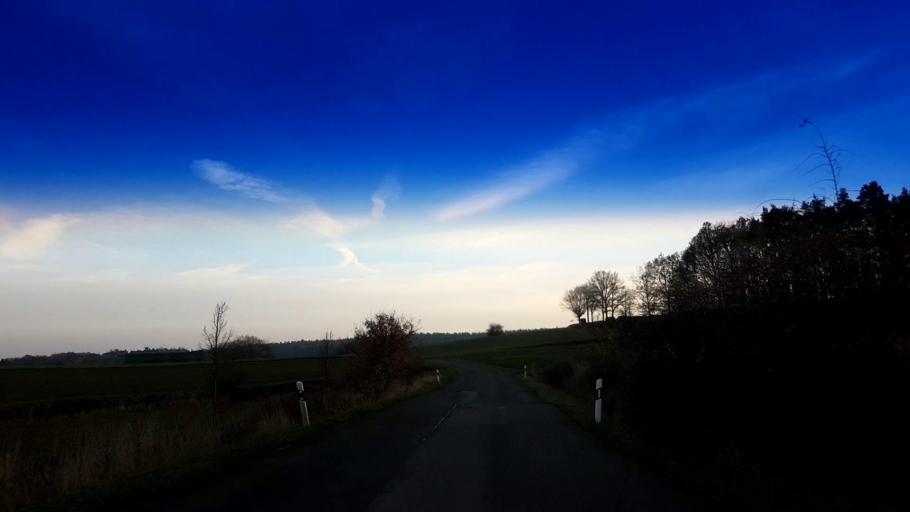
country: DE
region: Bavaria
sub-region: Upper Franconia
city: Stegaurach
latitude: 49.8635
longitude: 10.8201
